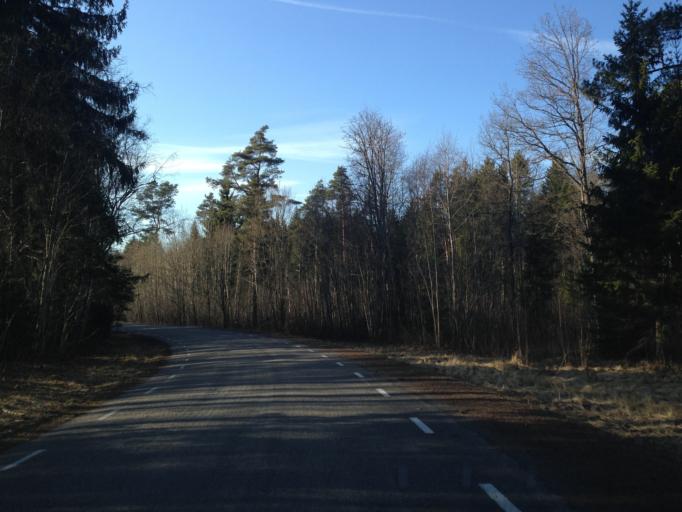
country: EE
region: Harju
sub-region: Nissi vald
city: Turba
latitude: 59.1441
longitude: 24.1581
